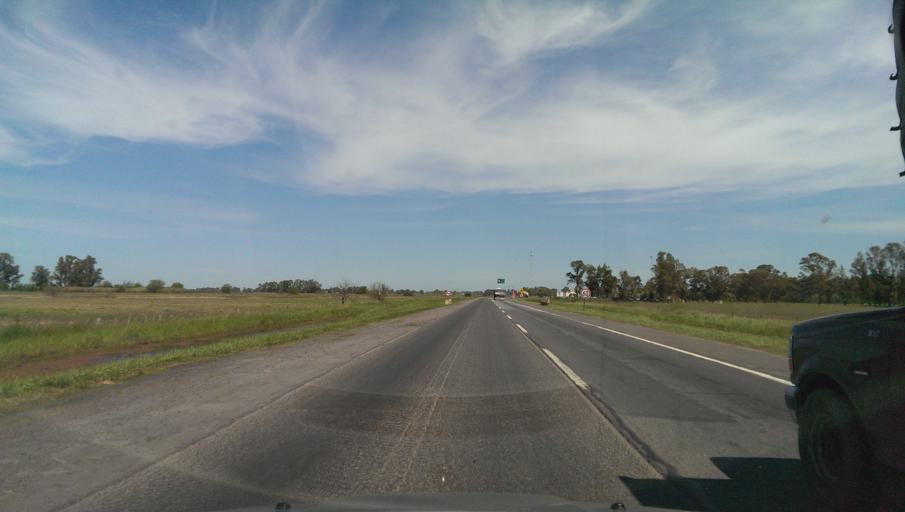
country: AR
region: Buenos Aires
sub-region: Partido de Las Flores
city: Las Flores
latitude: -36.0090
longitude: -59.0658
